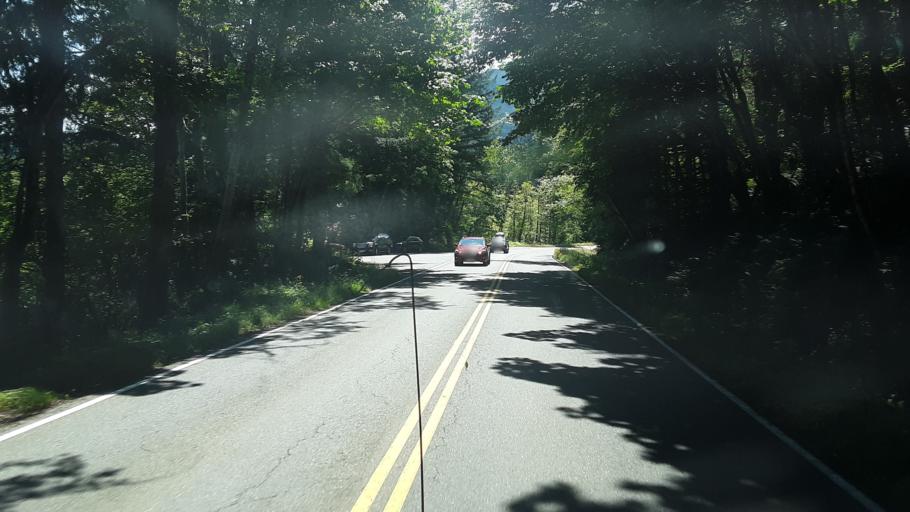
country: US
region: Washington
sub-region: Clark County
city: Yacolt
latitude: 46.0703
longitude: -122.1993
